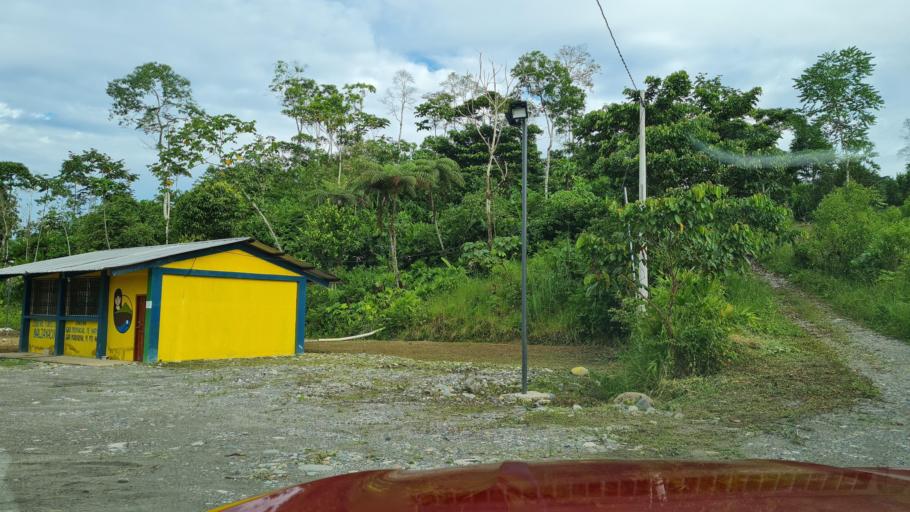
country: EC
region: Napo
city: Tena
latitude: -1.0483
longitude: -77.7779
